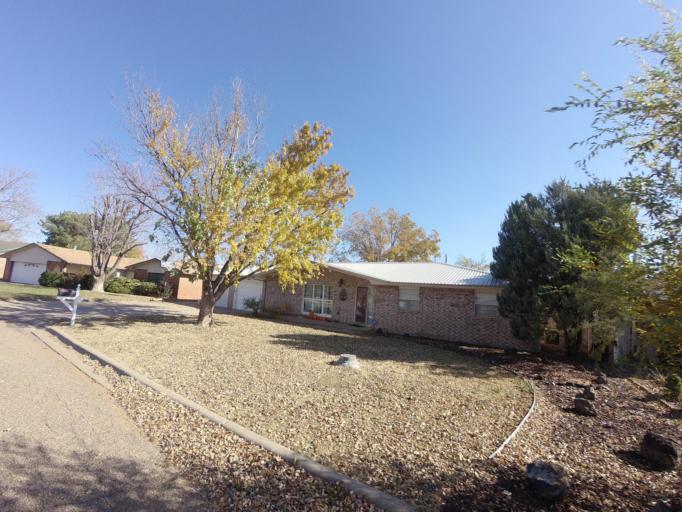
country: US
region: New Mexico
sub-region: Curry County
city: Clovis
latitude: 34.4125
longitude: -103.1832
